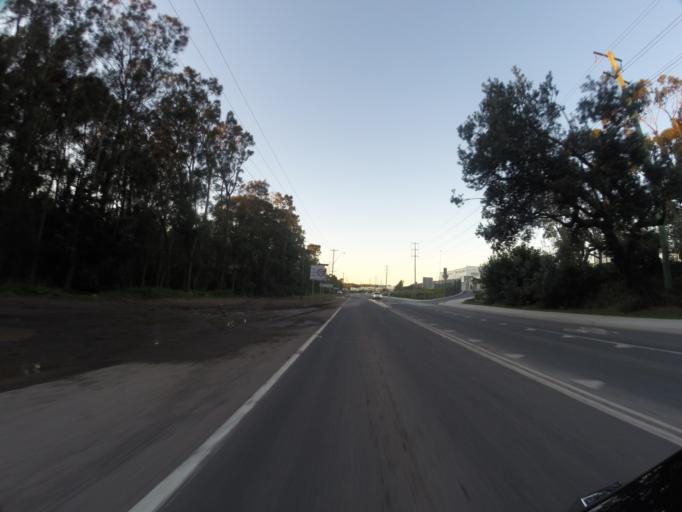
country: AU
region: New South Wales
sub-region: Sutherland Shire
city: Cronulla
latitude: -34.0381
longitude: 151.1580
